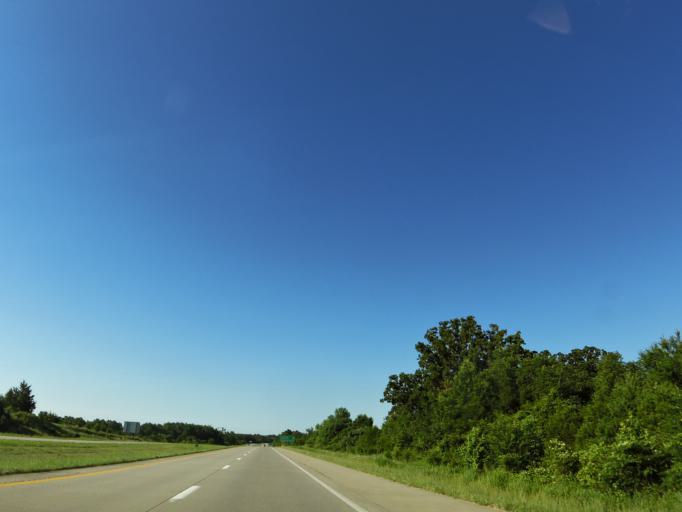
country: US
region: Missouri
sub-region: Butler County
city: Poplar Bluff
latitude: 36.7565
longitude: -90.4566
